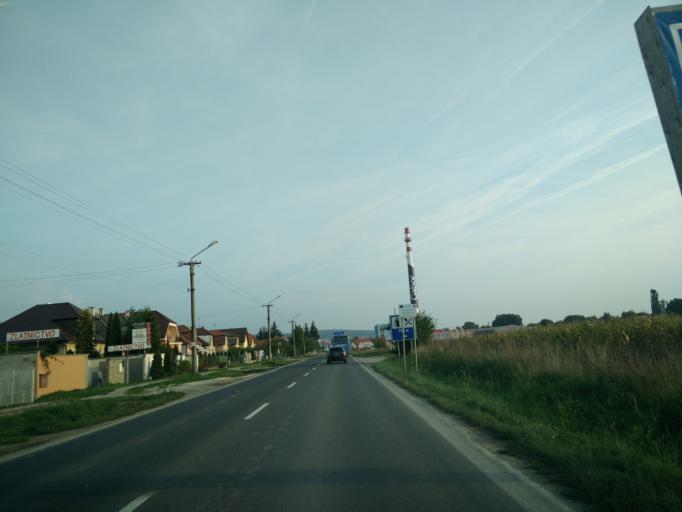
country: SK
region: Nitriansky
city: Banovce nad Bebravou
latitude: 48.7336
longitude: 18.2413
